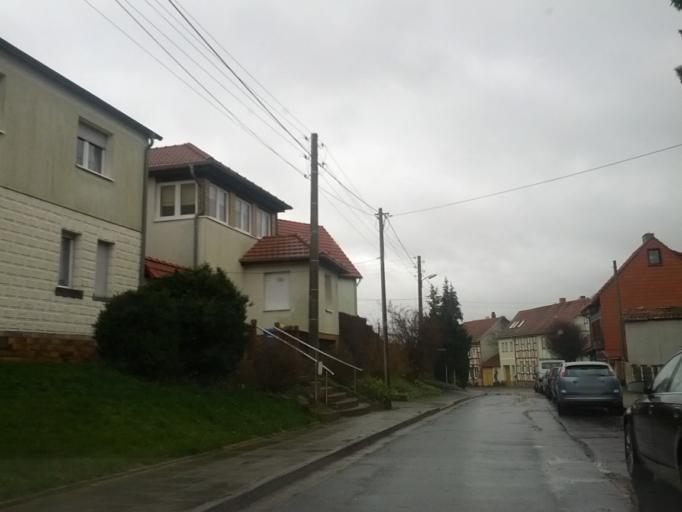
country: DE
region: Thuringia
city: Oberdorla
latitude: 51.1669
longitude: 10.4154
